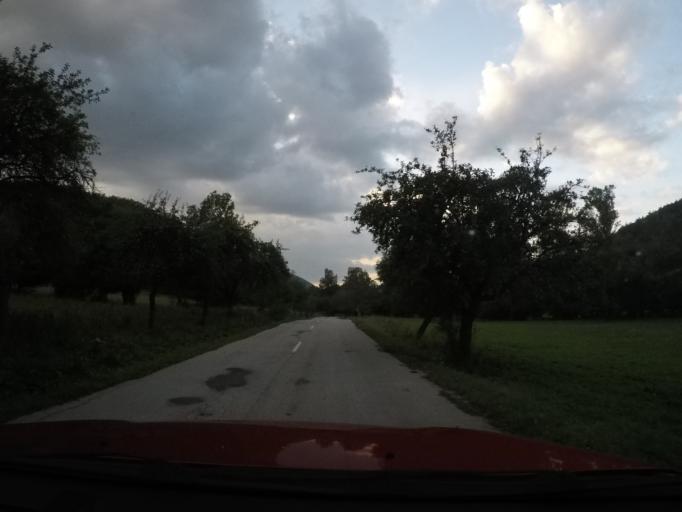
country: SK
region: Kosicky
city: Medzev
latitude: 48.6311
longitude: 20.7335
